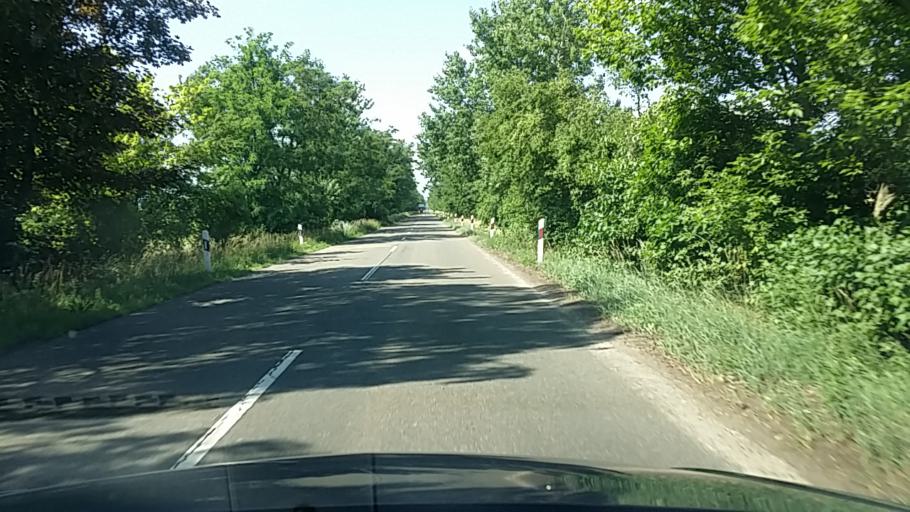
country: HU
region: Komarom-Esztergom
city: Esztergom
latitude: 47.8906
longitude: 18.7758
